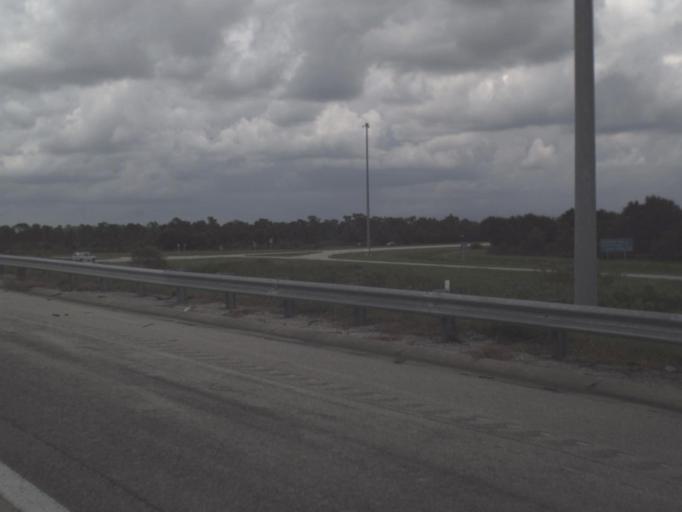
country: US
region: Florida
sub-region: Charlotte County
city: Harbour Heights
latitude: 26.9784
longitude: -82.0226
